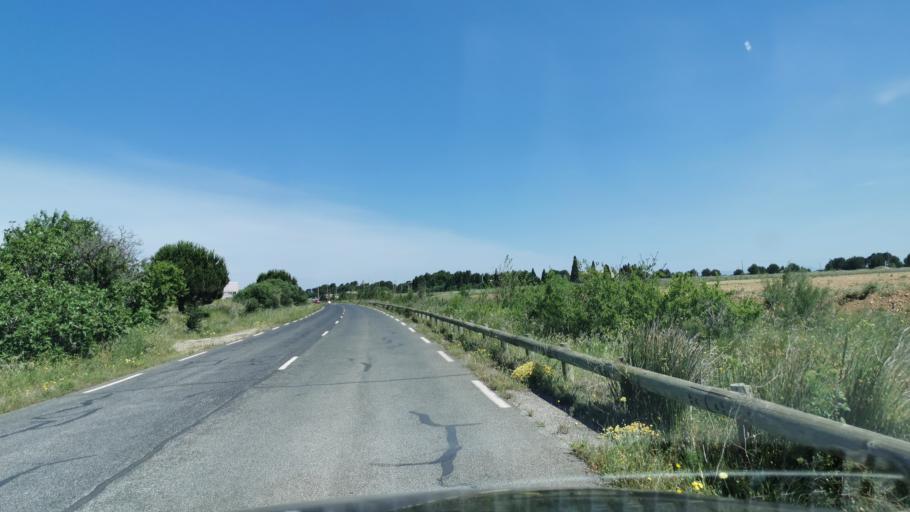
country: FR
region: Languedoc-Roussillon
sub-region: Departement de l'Aude
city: Narbonne
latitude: 43.1545
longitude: 2.9970
